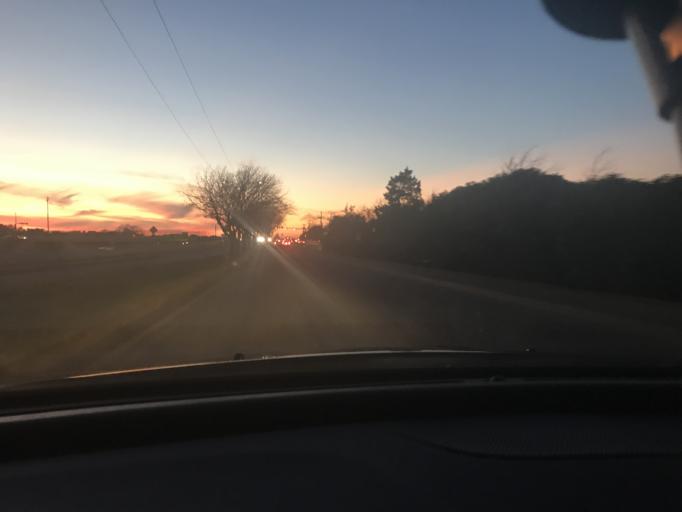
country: US
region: Texas
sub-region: Tarrant County
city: Arlington
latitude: 32.7603
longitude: -97.1120
